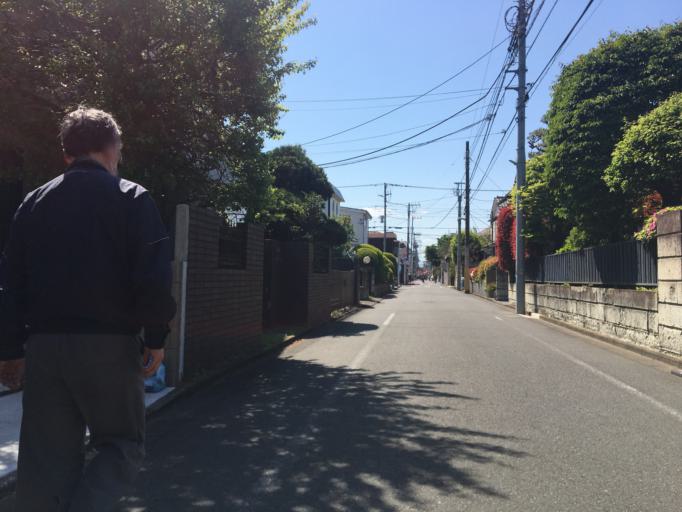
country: JP
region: Tokyo
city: Kokubunji
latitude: 35.7240
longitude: 139.4836
